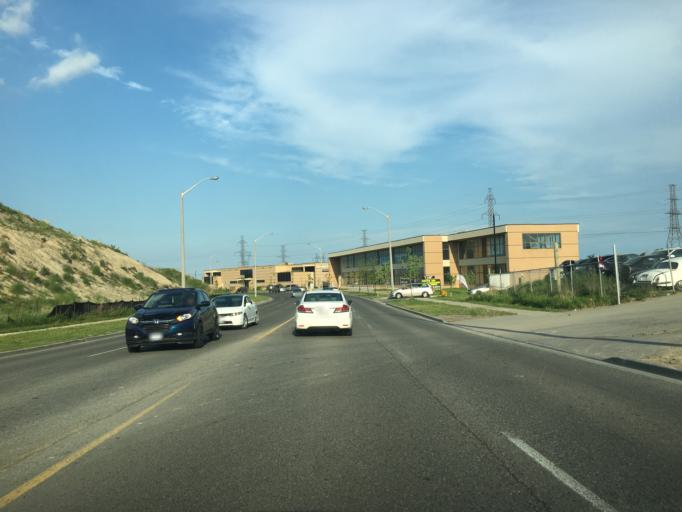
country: CA
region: Ontario
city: Markham
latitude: 43.8266
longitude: -79.2386
